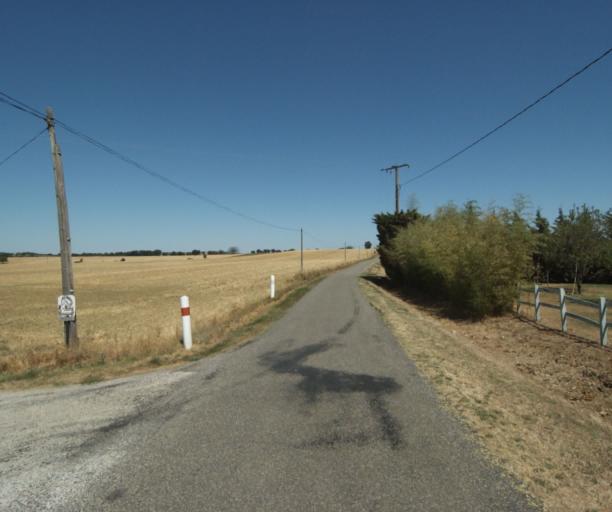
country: FR
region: Midi-Pyrenees
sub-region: Departement de la Haute-Garonne
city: Saint-Felix-Lauragais
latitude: 43.4627
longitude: 1.9051
